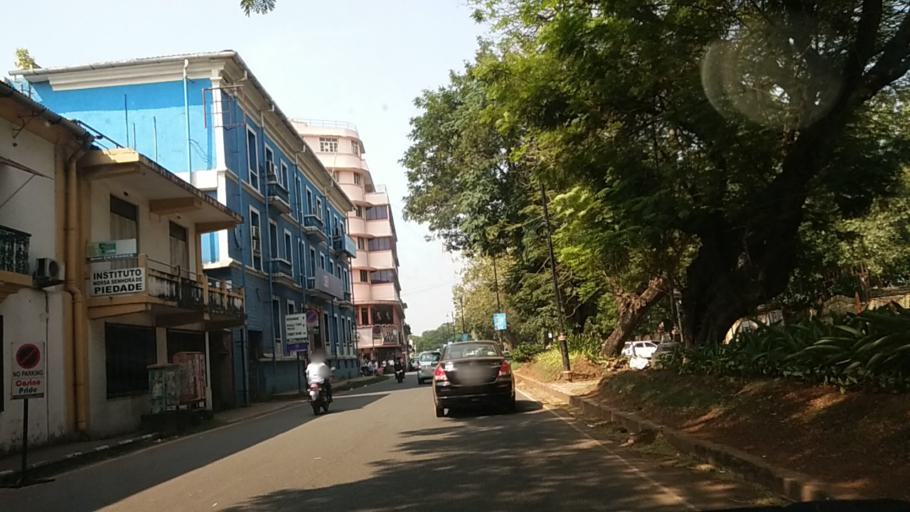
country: IN
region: Goa
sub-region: North Goa
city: Panaji
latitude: 15.5012
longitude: 73.8275
